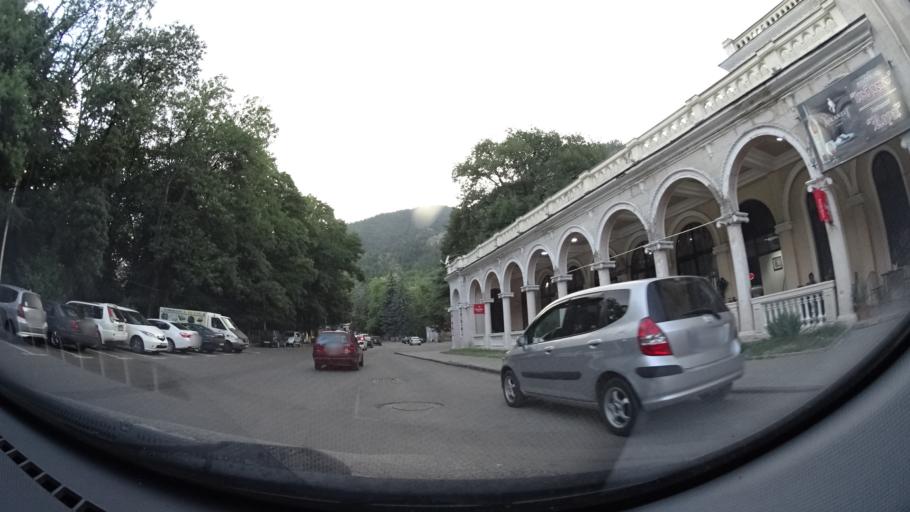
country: GE
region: Samtskhe-Javakheti
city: Borjomi
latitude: 41.8413
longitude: 43.3850
